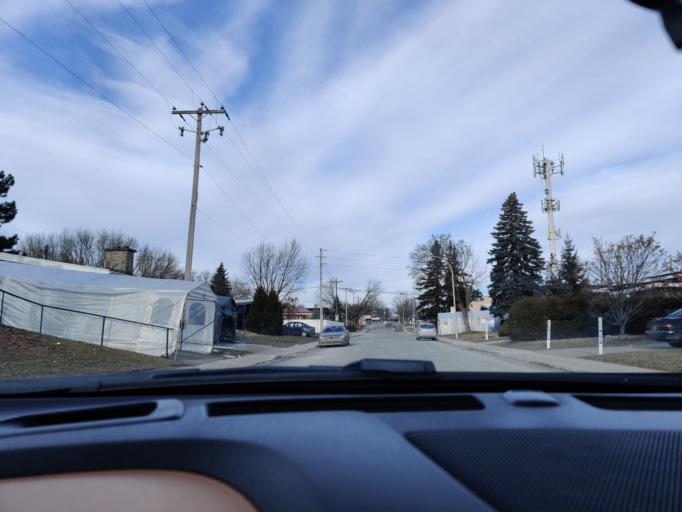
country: CA
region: Quebec
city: Dollard-Des Ormeaux
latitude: 45.5268
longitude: -73.7567
